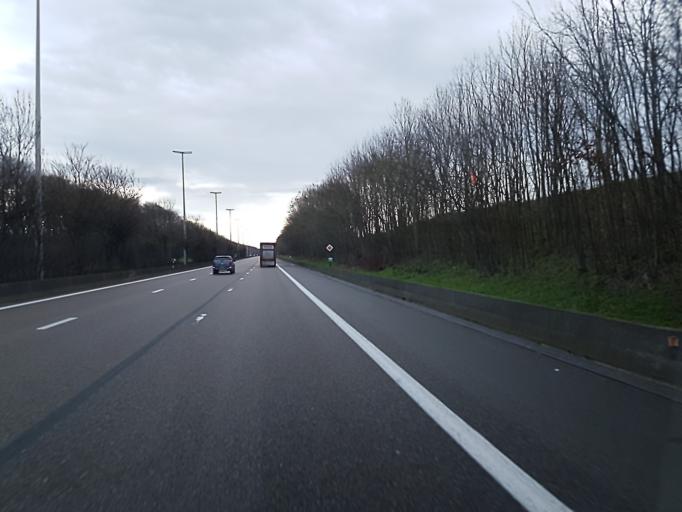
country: BE
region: Flanders
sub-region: Provincie Vlaams-Brabant
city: Boutersem
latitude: 50.8239
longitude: 4.8262
